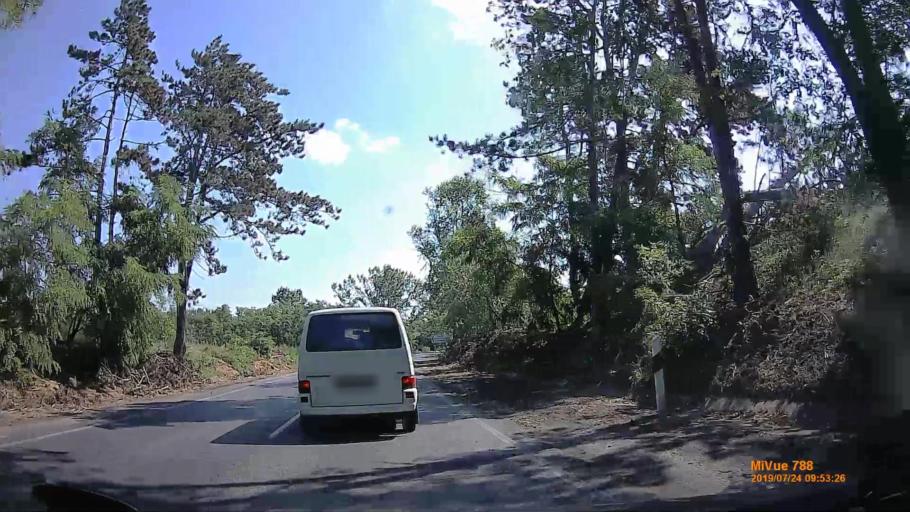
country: HU
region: Szabolcs-Szatmar-Bereg
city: Nyirmada
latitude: 48.0505
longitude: 22.1969
